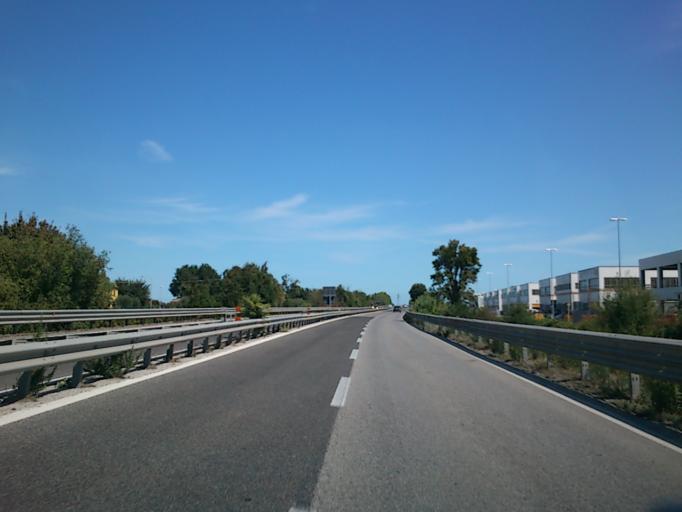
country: IT
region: The Marches
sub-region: Provincia di Pesaro e Urbino
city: Bellocchi
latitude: 43.7906
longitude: 12.9981
